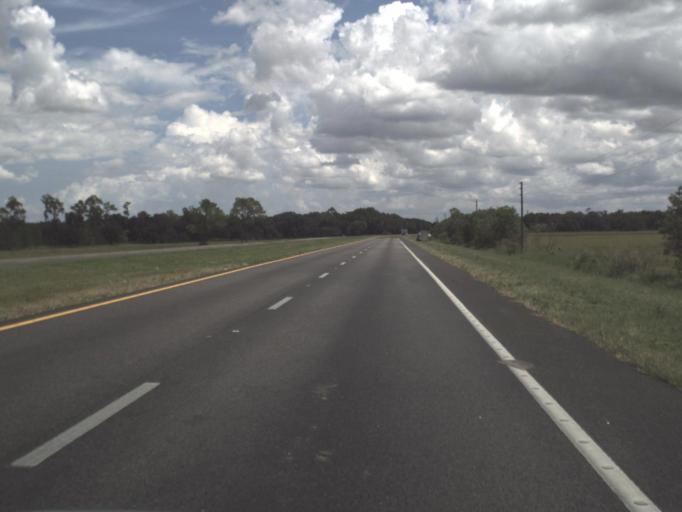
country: US
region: Florida
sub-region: Polk County
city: Alturas
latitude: 27.9117
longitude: -81.6904
